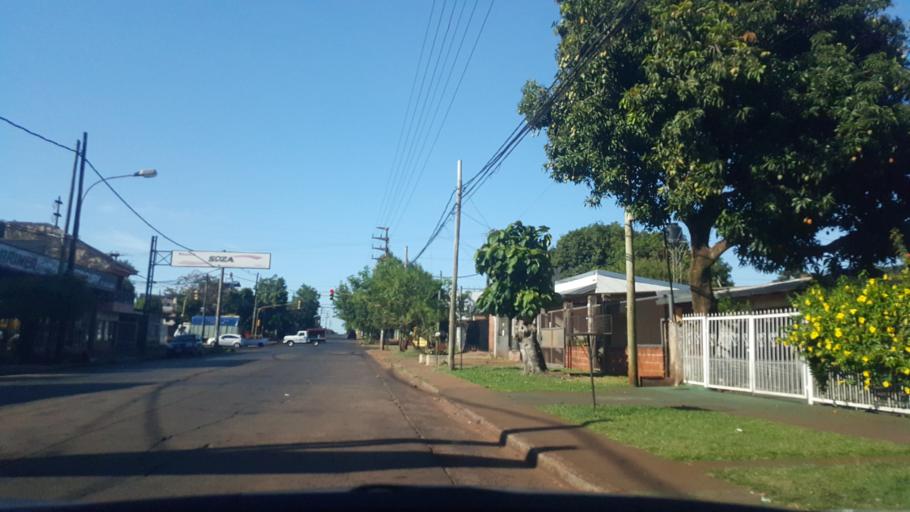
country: AR
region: Misiones
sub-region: Departamento de Capital
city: Posadas
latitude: -27.3772
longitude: -55.9103
